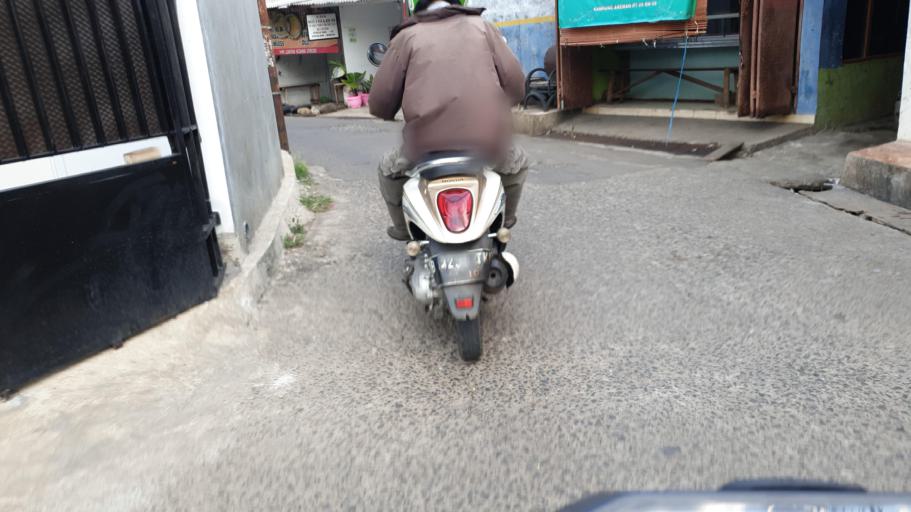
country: ID
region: West Java
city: Depok
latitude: -6.3684
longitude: 106.8507
